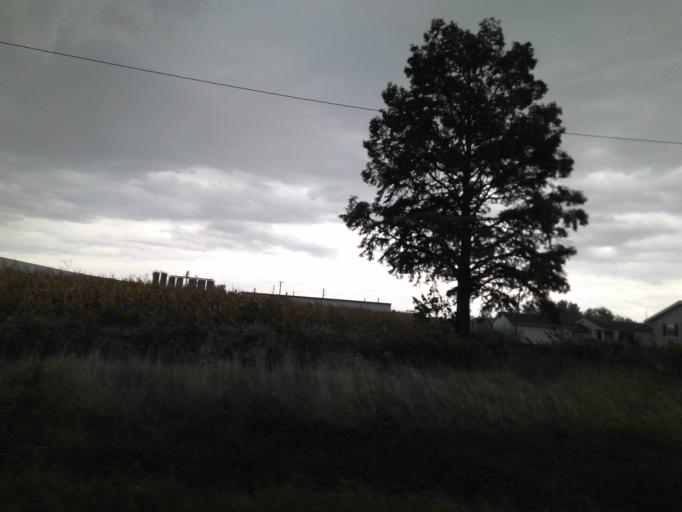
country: US
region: Illinois
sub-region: Bond County
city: Greenville
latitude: 38.8811
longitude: -89.3907
